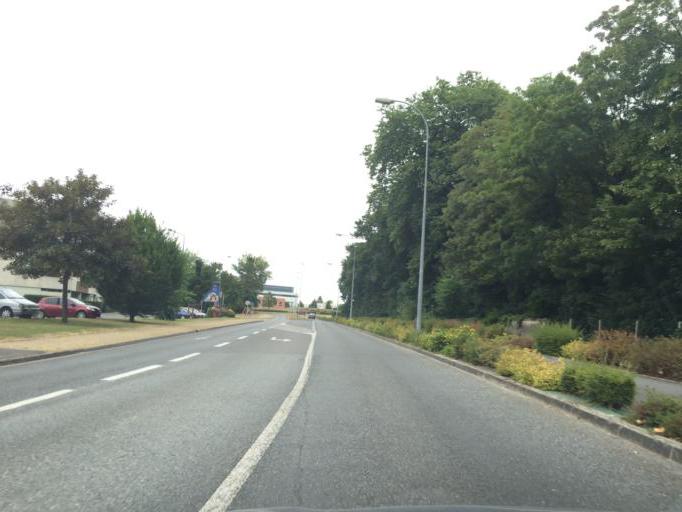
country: FR
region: Auvergne
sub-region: Departement de l'Allier
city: Moulins
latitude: 46.5390
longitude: 3.3353
